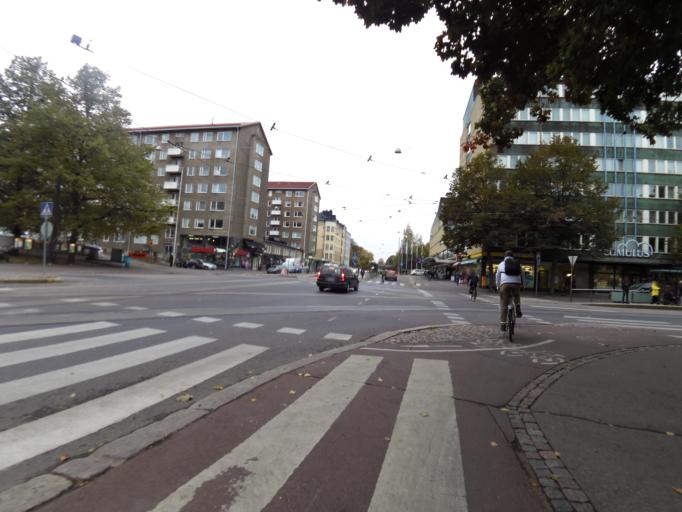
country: FI
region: Uusimaa
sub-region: Helsinki
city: Helsinki
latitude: 60.1866
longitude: 24.9490
